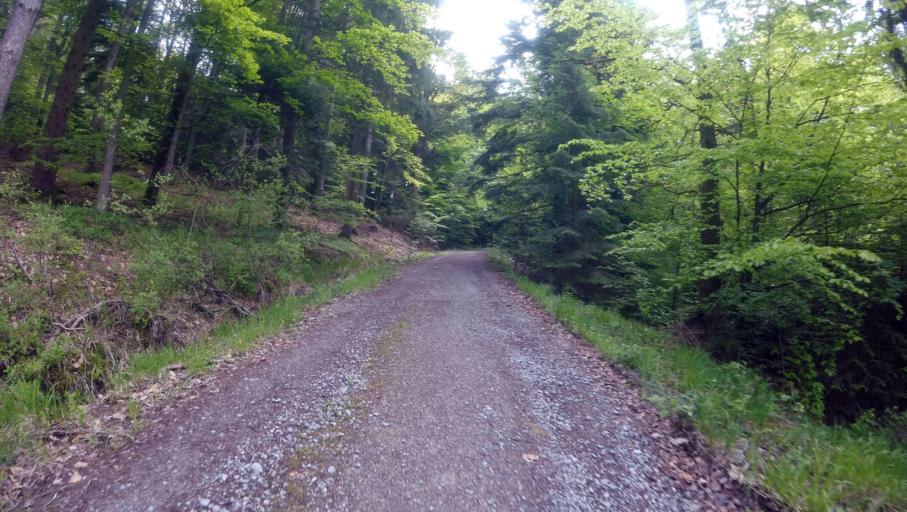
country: DE
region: Baden-Wuerttemberg
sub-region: Regierungsbezirk Stuttgart
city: Kaisersbach
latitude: 48.9186
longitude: 9.6135
